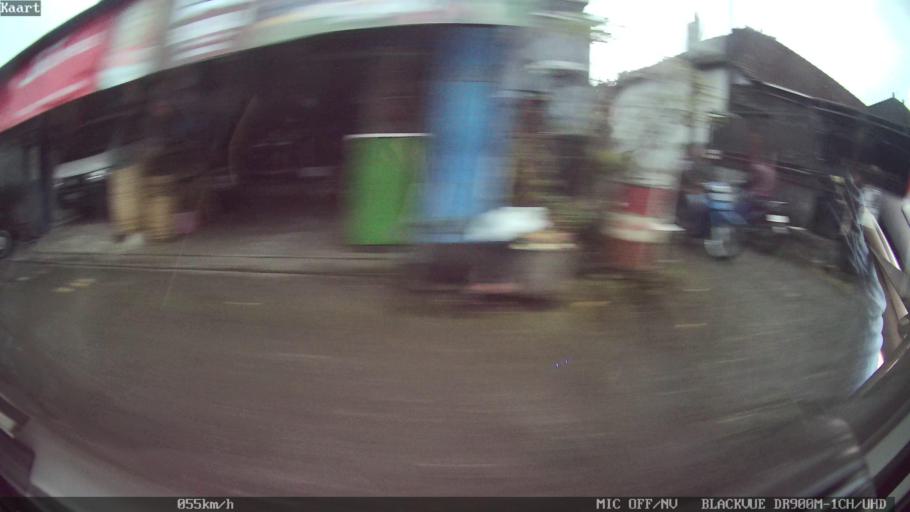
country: ID
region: Bali
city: Empalan
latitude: -8.4004
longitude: 115.1480
